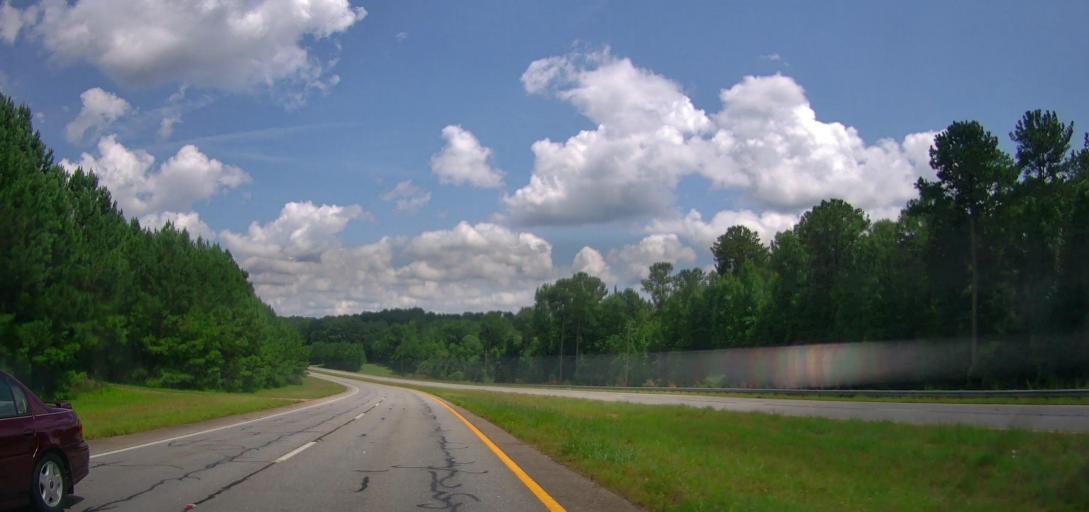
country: US
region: Georgia
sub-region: Heard County
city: Franklin
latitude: 33.2597
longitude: -85.0646
